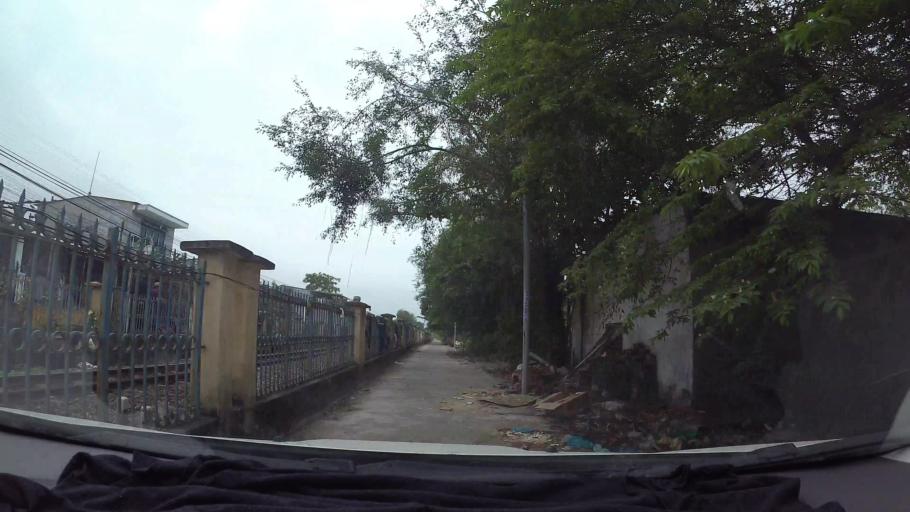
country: VN
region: Da Nang
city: Lien Chieu
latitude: 16.0771
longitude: 108.1541
